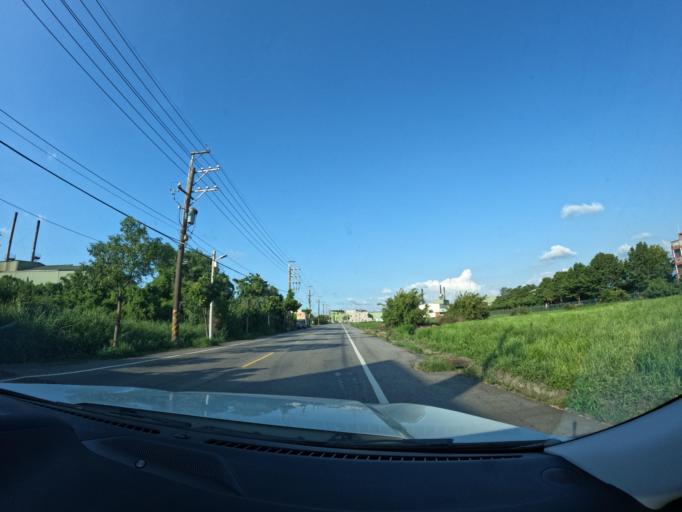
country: TW
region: Taiwan
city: Taoyuan City
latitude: 25.0053
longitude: 121.1289
